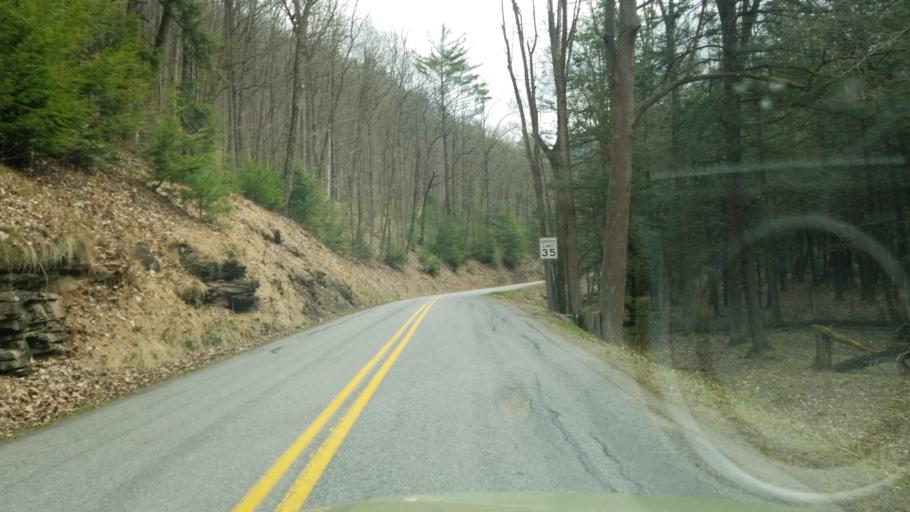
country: US
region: Pennsylvania
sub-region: Cameron County
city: Emporium
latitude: 41.2826
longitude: -78.1350
